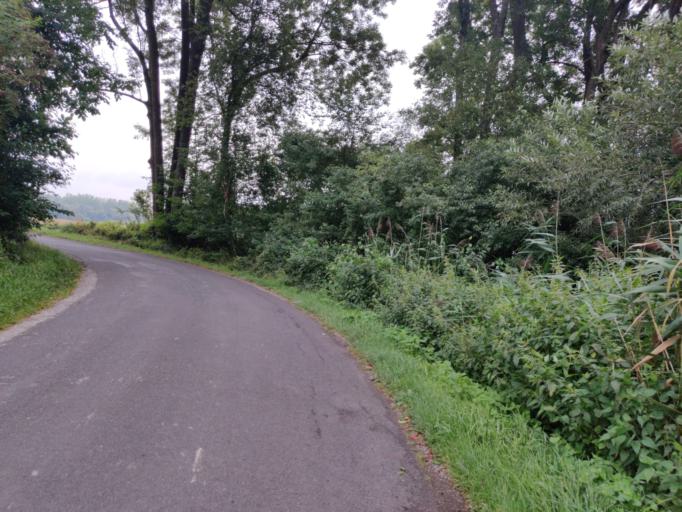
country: AT
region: Upper Austria
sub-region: Politischer Bezirk Linz-Land
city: Asten
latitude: 48.2311
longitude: 14.4368
